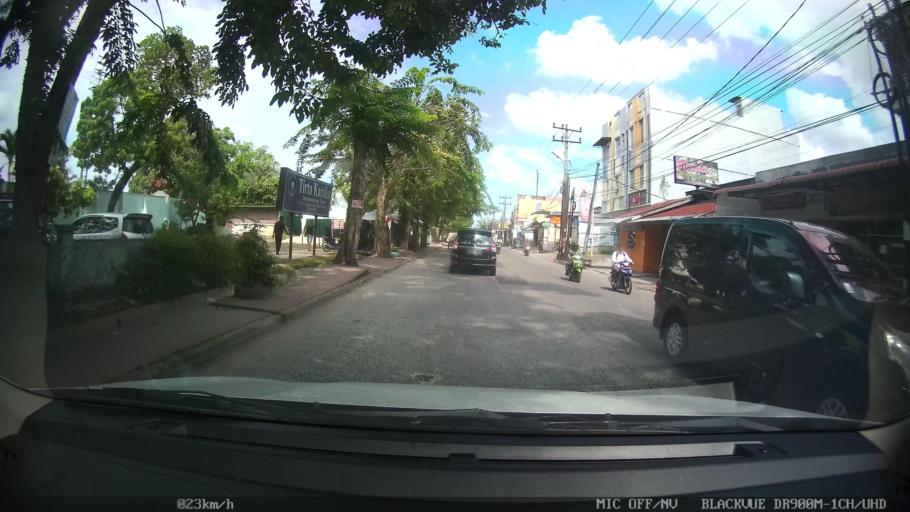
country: ID
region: North Sumatra
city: Medan
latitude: 3.6049
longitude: 98.6396
